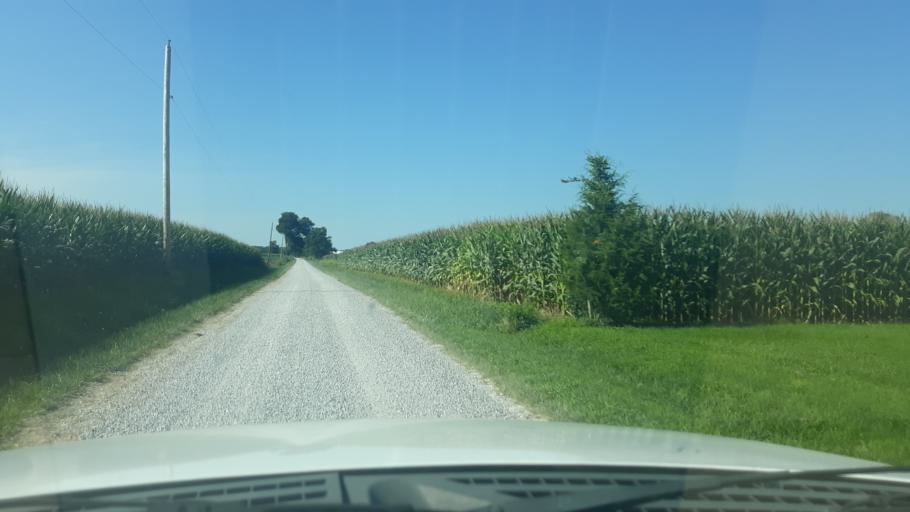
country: US
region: Illinois
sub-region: Saline County
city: Eldorado
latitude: 37.8582
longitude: -88.4850
